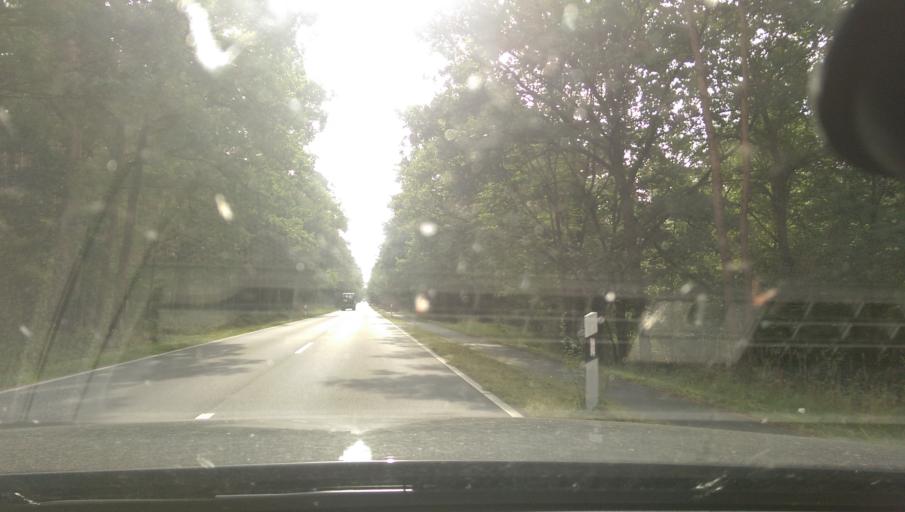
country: DE
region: Lower Saxony
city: Wietze
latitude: 52.6750
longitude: 9.8527
